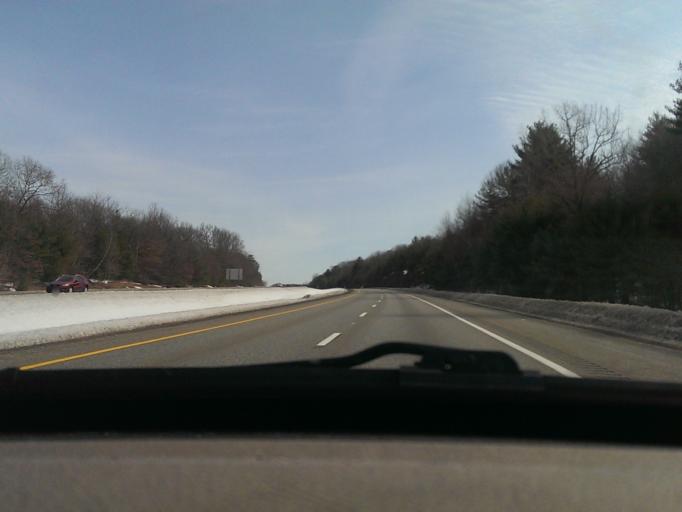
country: US
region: Massachusetts
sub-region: Worcester County
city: Millville
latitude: 42.0317
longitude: -71.6185
